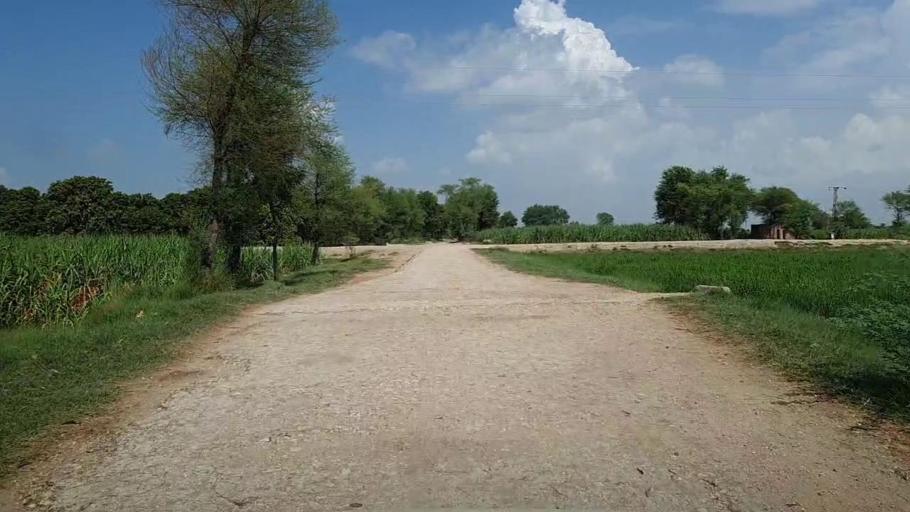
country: PK
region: Sindh
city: Bhiria
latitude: 26.9176
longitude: 68.2368
